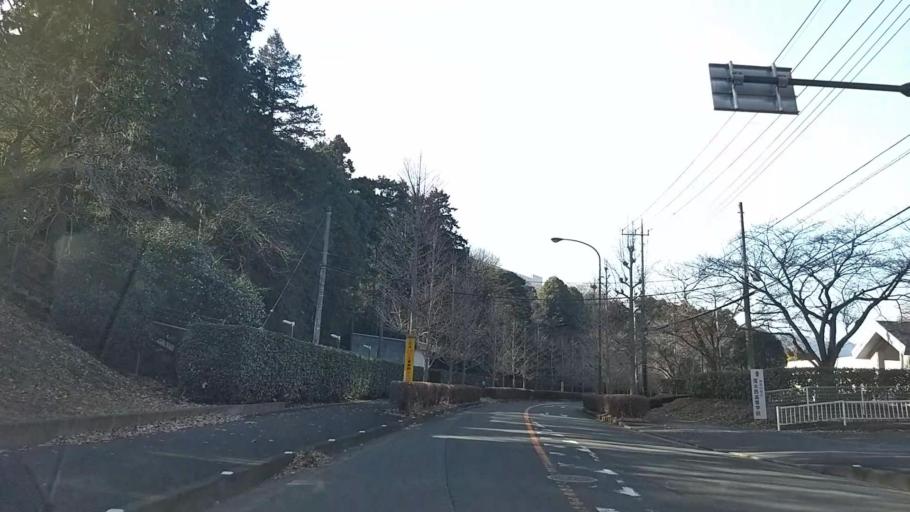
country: JP
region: Kanagawa
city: Atsugi
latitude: 35.4458
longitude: 139.3159
